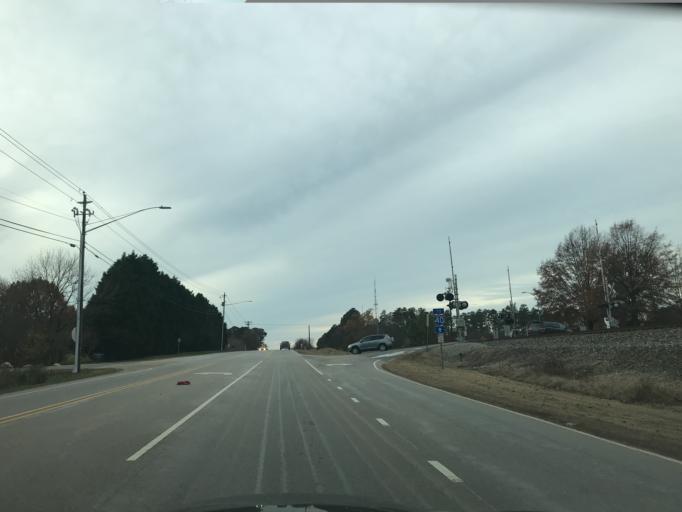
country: US
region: North Carolina
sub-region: Wake County
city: Cary
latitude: 35.7898
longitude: -78.7498
